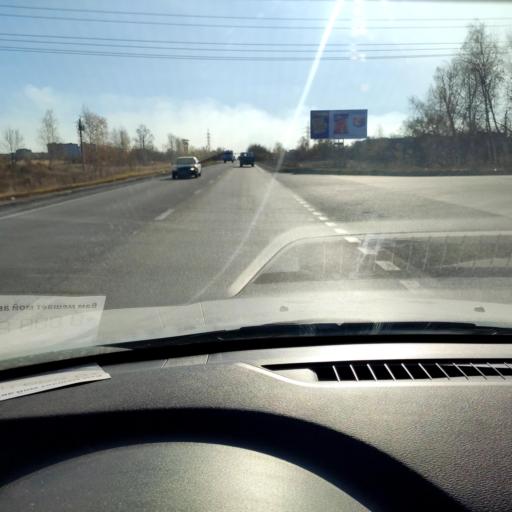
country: RU
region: Samara
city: Tol'yatti
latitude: 53.5486
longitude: 49.3753
